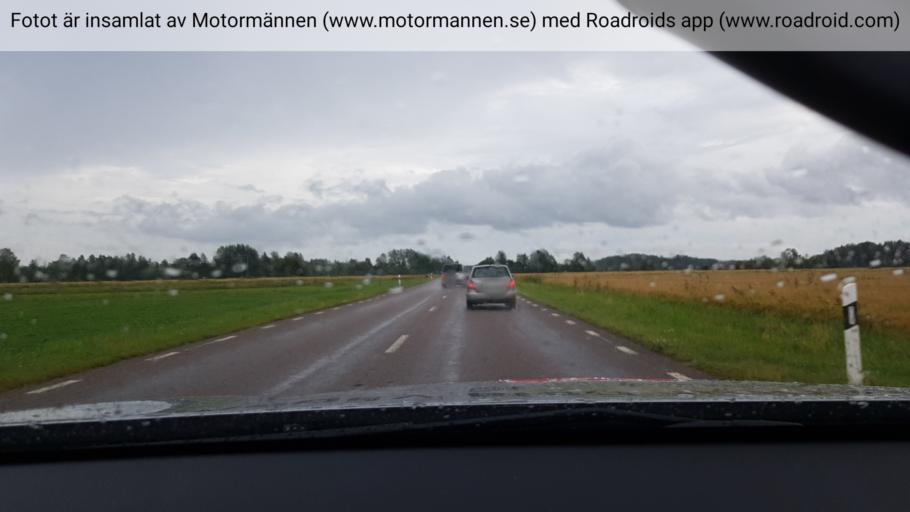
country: SE
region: Uppsala
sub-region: Tierps Kommun
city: Karlholmsbruk
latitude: 60.4950
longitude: 17.7016
